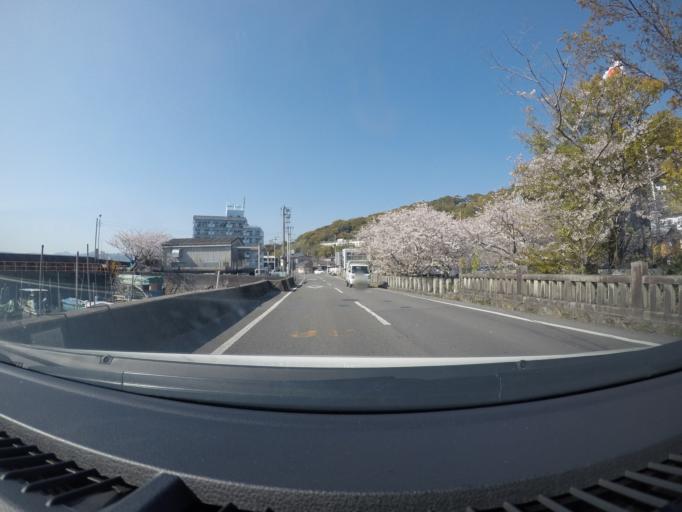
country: JP
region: Kochi
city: Kochi-shi
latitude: 33.5454
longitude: 133.5702
